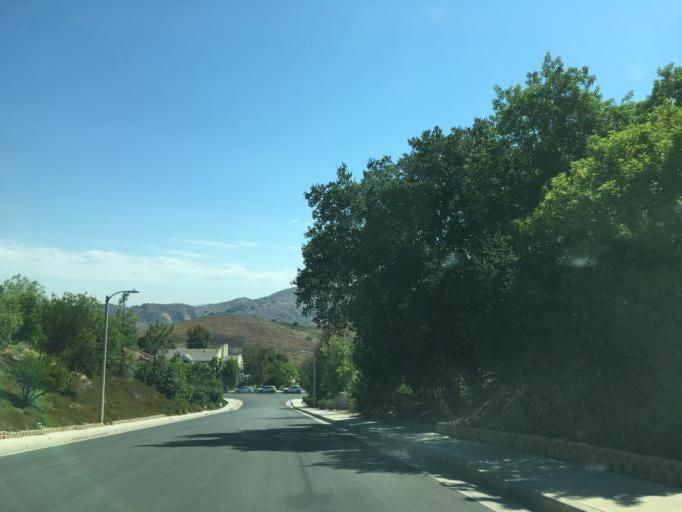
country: US
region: California
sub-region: Los Angeles County
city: Agoura
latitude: 34.1304
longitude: -118.7184
